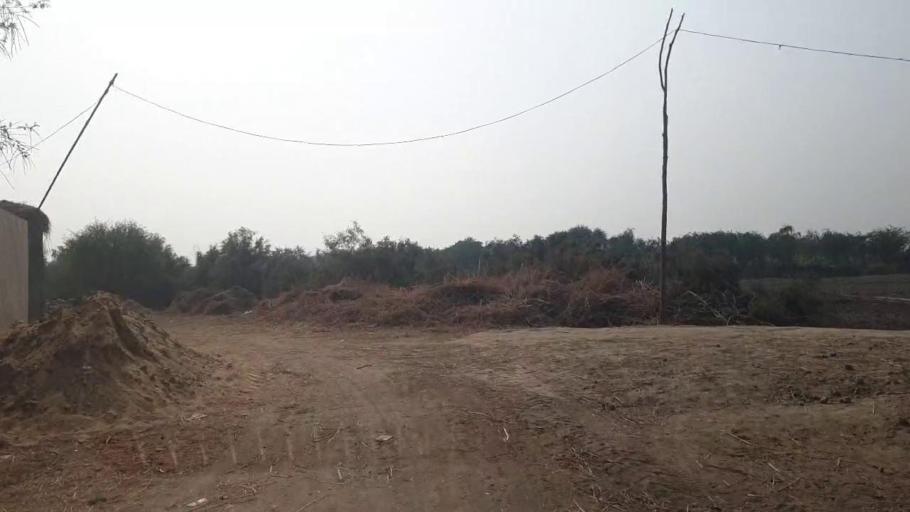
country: PK
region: Sindh
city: Tando Muhammad Khan
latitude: 25.2724
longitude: 68.4915
